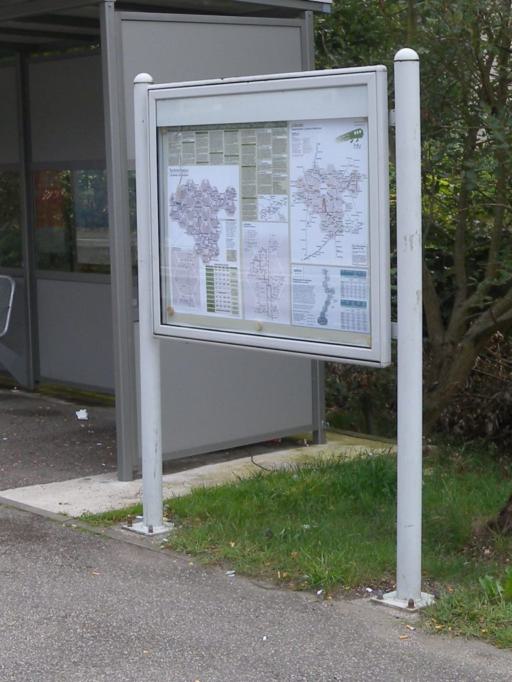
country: DE
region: Baden-Wuerttemberg
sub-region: Regierungsbezirk Stuttgart
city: Heidenheim an der Brenz
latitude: 48.7081
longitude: 10.1588
